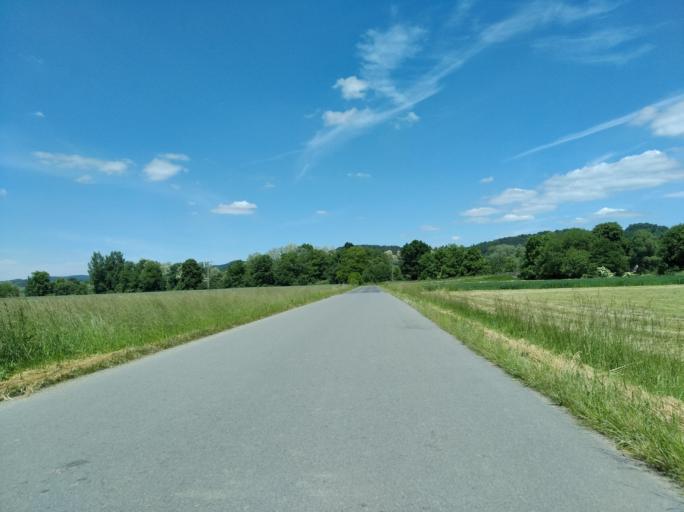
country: PL
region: Subcarpathian Voivodeship
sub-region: Powiat krosnienski
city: Wojaszowka
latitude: 49.7830
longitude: 21.6795
